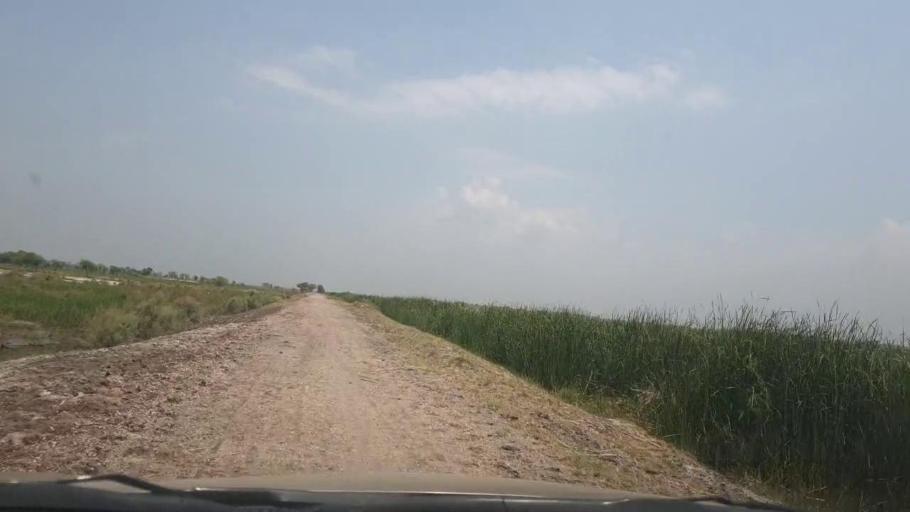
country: PK
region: Sindh
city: Naudero
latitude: 27.7191
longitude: 68.2995
